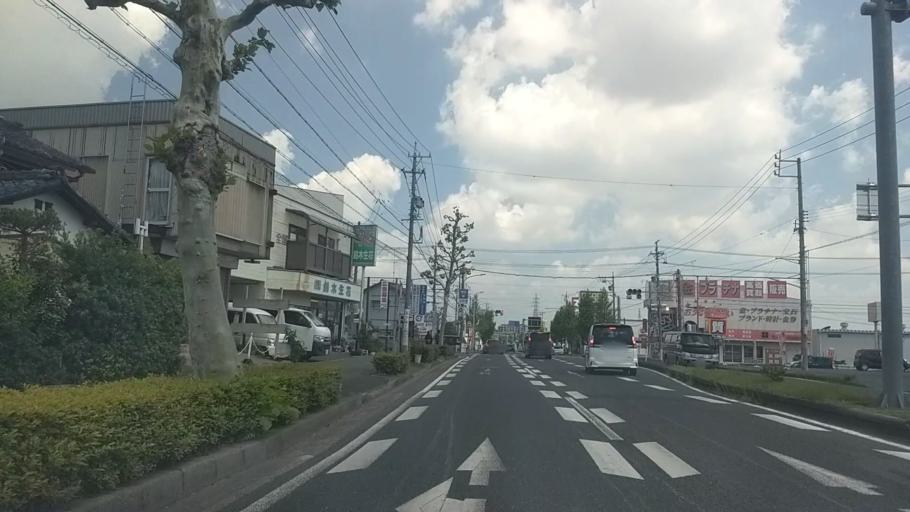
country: JP
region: Shizuoka
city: Hamamatsu
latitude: 34.7313
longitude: 137.7335
